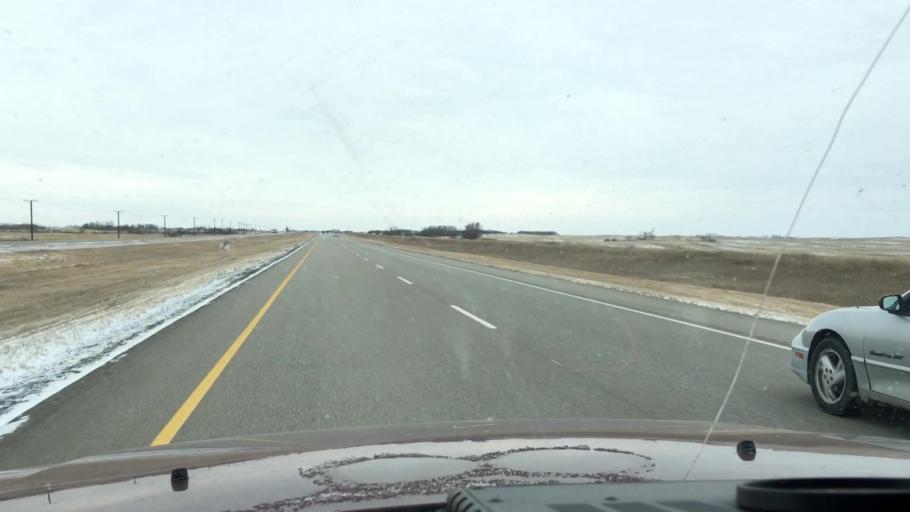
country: CA
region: Saskatchewan
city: Watrous
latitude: 51.4005
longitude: -106.1766
